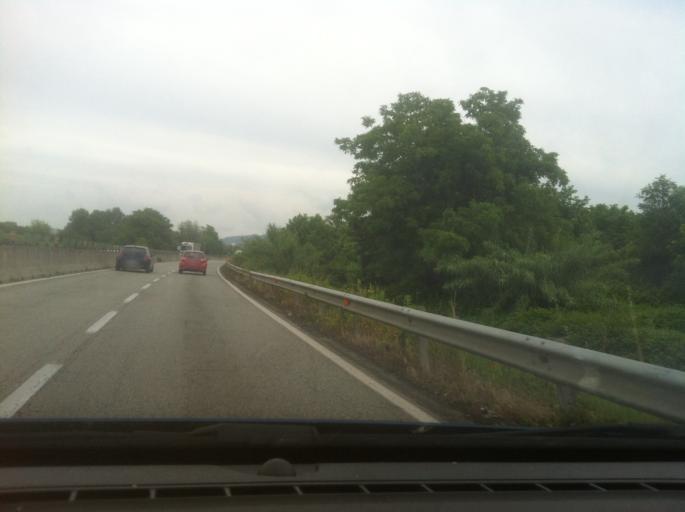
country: IT
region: Piedmont
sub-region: Provincia di Torino
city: Settimo Torinese
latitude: 45.1302
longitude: 7.7765
